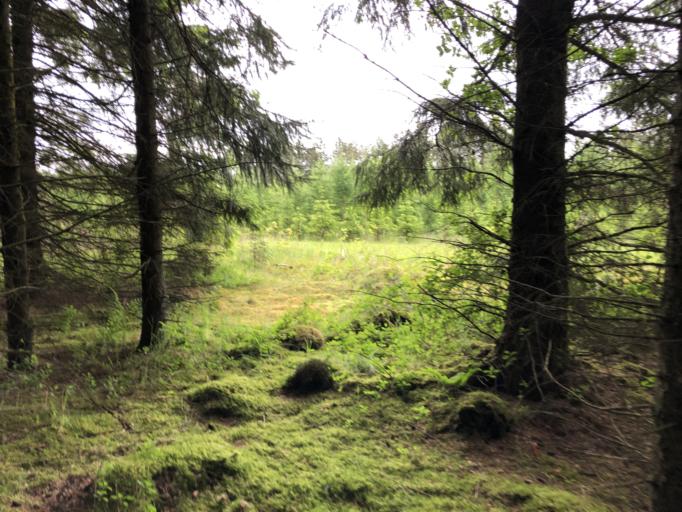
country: DK
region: Central Jutland
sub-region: Holstebro Kommune
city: Ulfborg
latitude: 56.2798
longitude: 8.3723
